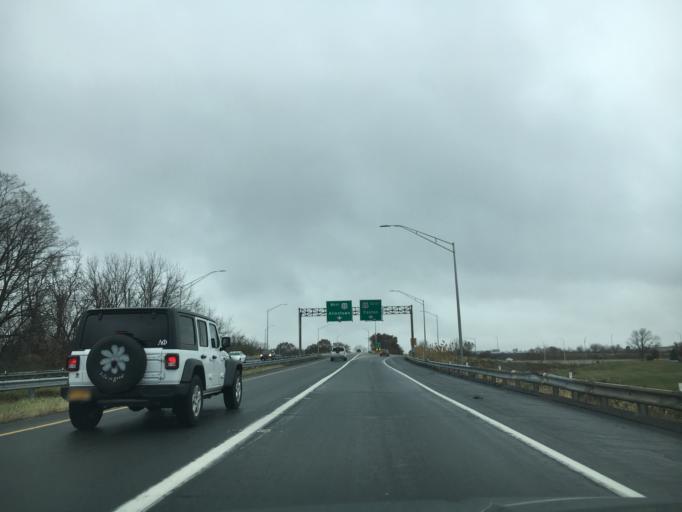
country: US
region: Pennsylvania
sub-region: Northampton County
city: Bethlehem
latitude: 40.6457
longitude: -75.4129
